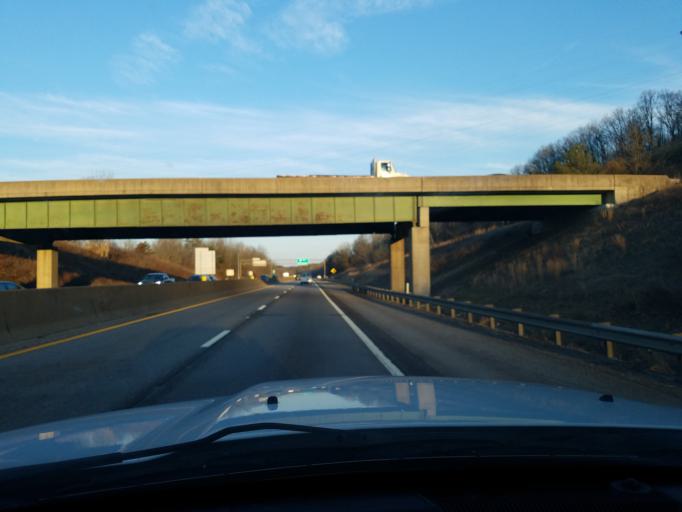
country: US
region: West Virginia
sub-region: Kanawha County
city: Nitro
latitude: 38.4480
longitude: -81.8486
